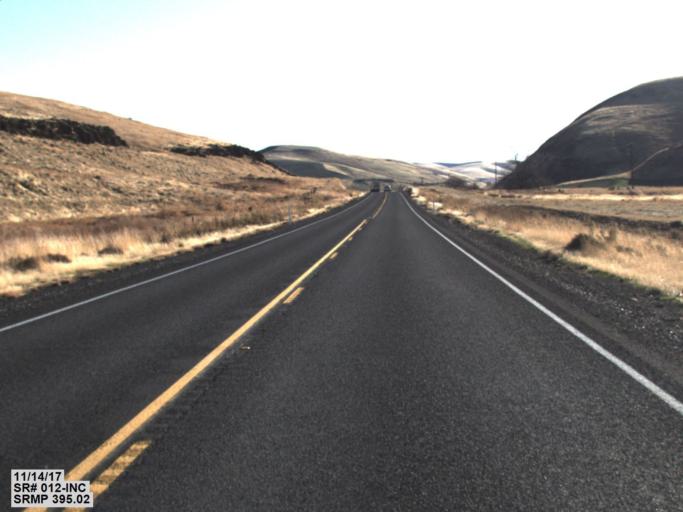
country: US
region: Washington
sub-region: Garfield County
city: Pomeroy
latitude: 46.4884
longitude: -117.7585
